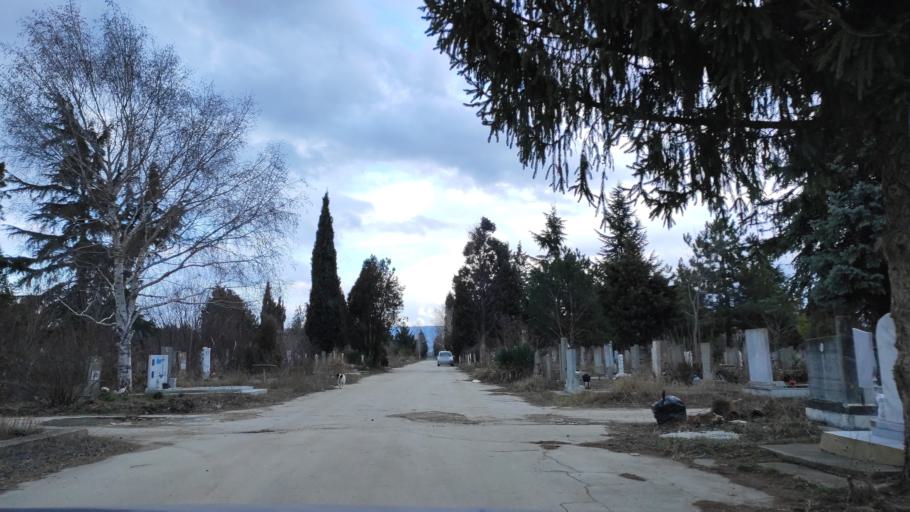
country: BG
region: Varna
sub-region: Obshtina Aksakovo
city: Aksakovo
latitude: 43.2199
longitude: 27.8090
